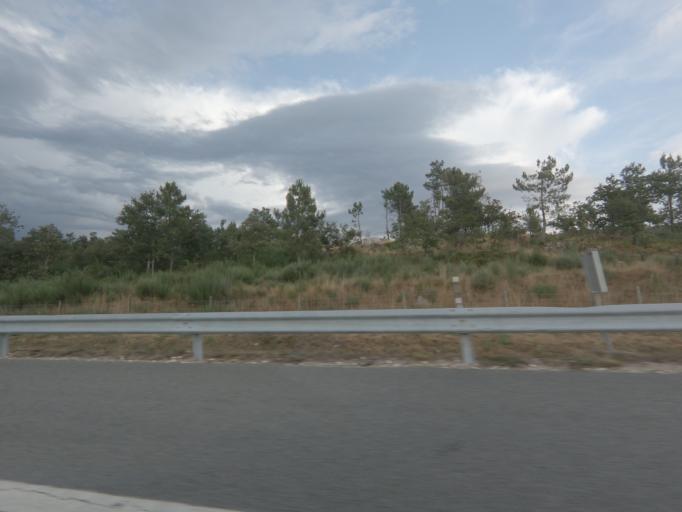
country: PT
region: Viseu
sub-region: Castro Daire
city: Castro Daire
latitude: 40.9842
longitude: -7.8823
